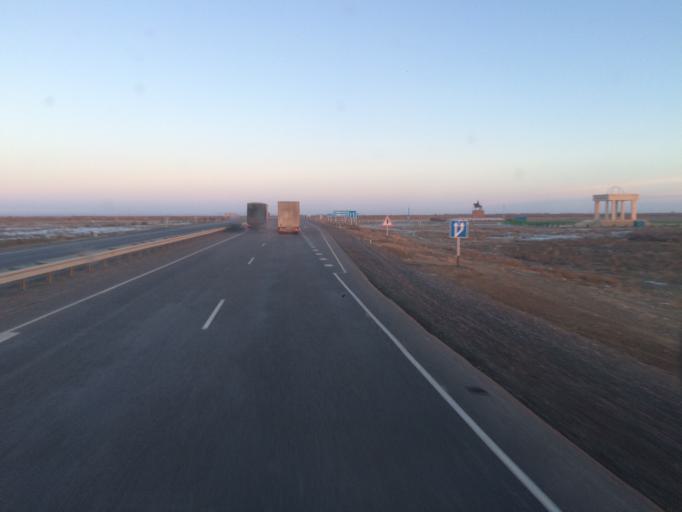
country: KZ
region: Qyzylorda
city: Zhangaqorghan
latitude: 44.1028
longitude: 67.0527
